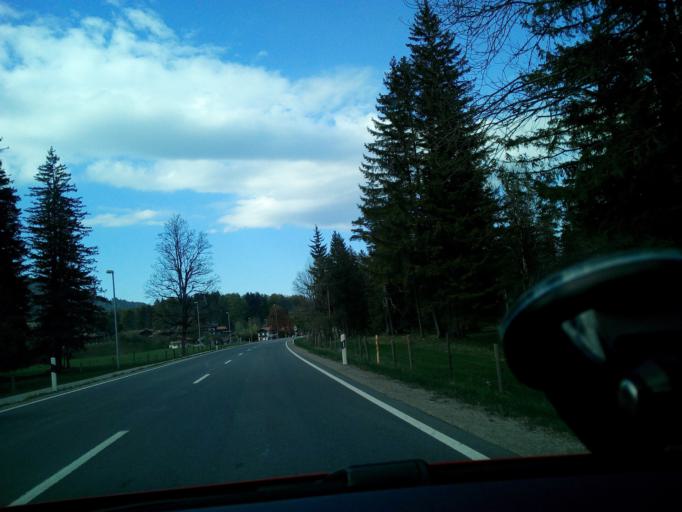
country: DE
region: Bavaria
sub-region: Upper Bavaria
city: Kreuth
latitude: 47.6506
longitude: 11.7466
